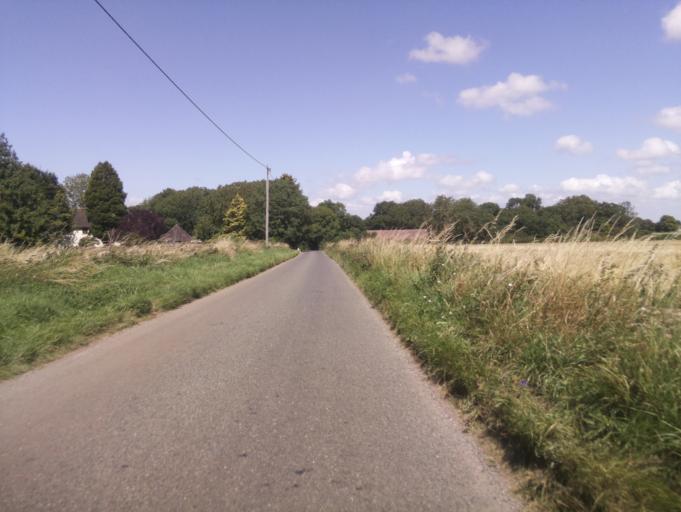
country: GB
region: England
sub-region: Wiltshire
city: Norton
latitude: 51.5215
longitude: -2.1320
